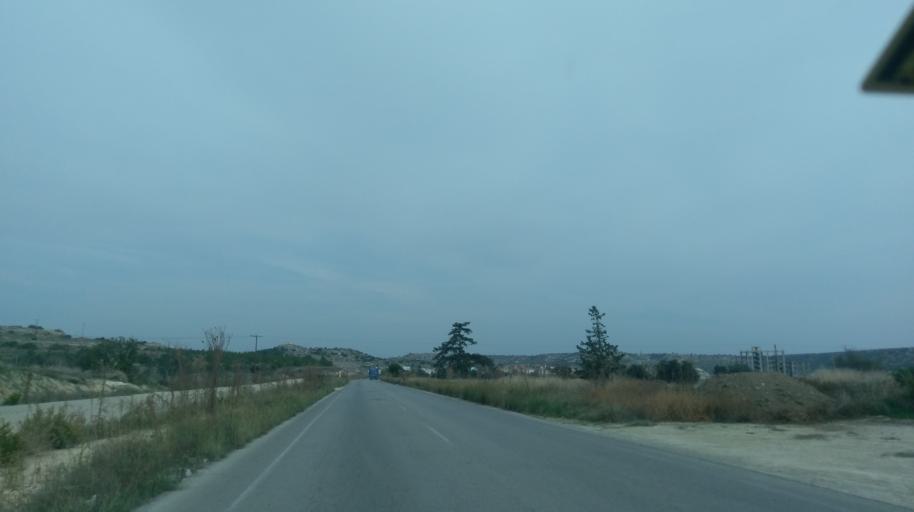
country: CY
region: Ammochostos
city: Trikomo
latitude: 35.3363
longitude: 33.9807
